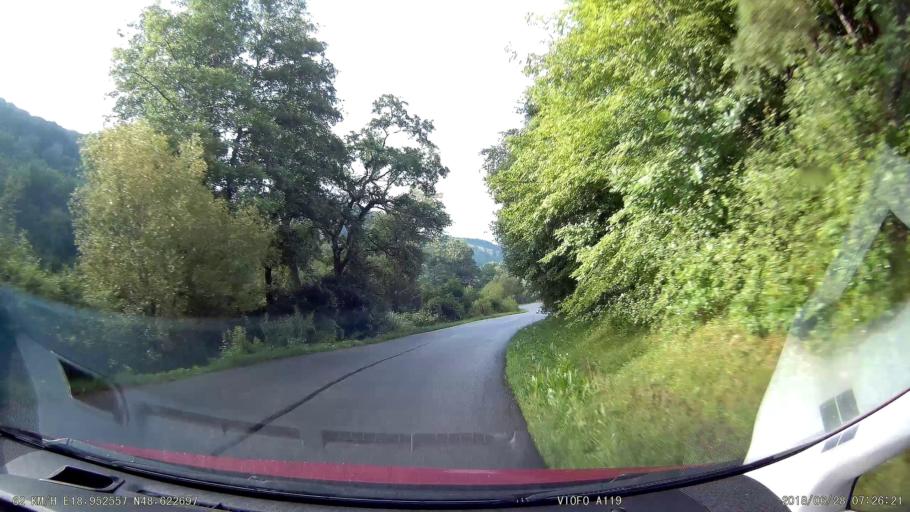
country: SK
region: Banskobystricky
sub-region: Okres Ziar nad Hronom
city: Kremnica
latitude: 48.6225
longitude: 18.9527
